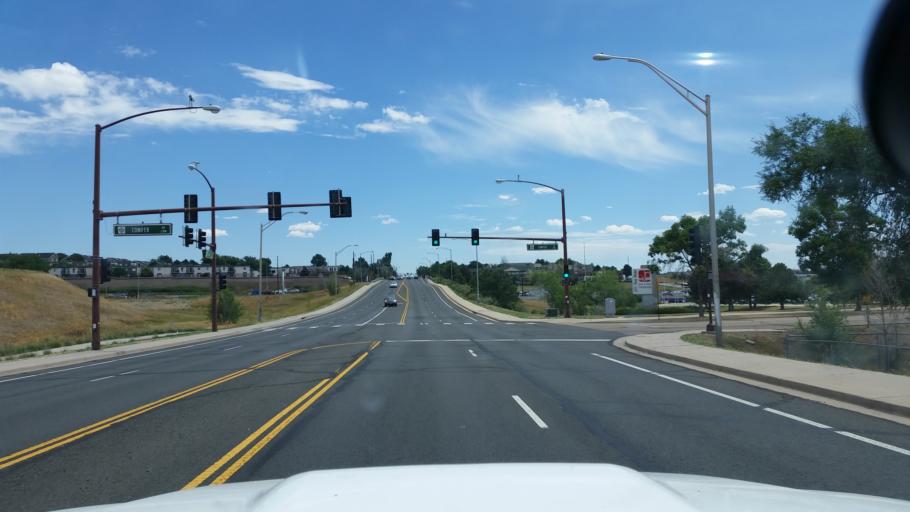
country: US
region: Colorado
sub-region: Adams County
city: Federal Heights
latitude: 39.8563
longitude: -104.9907
